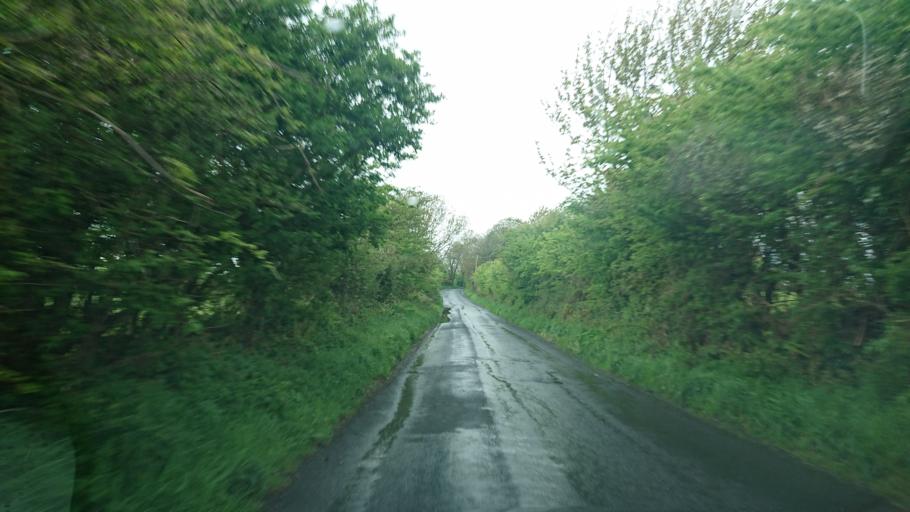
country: IE
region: Munster
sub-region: Waterford
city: Waterford
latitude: 52.2248
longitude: -7.0724
